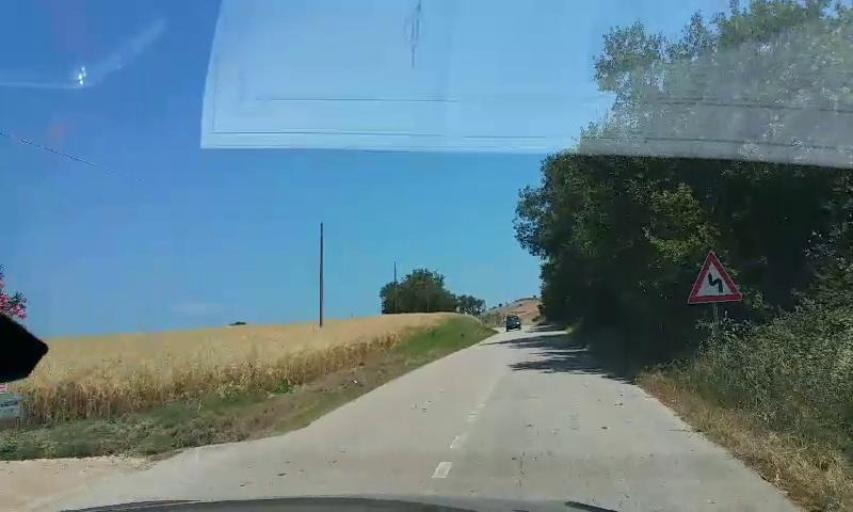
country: IT
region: Molise
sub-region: Provincia di Campobasso
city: Guglionesi
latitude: 41.9458
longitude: 14.8992
